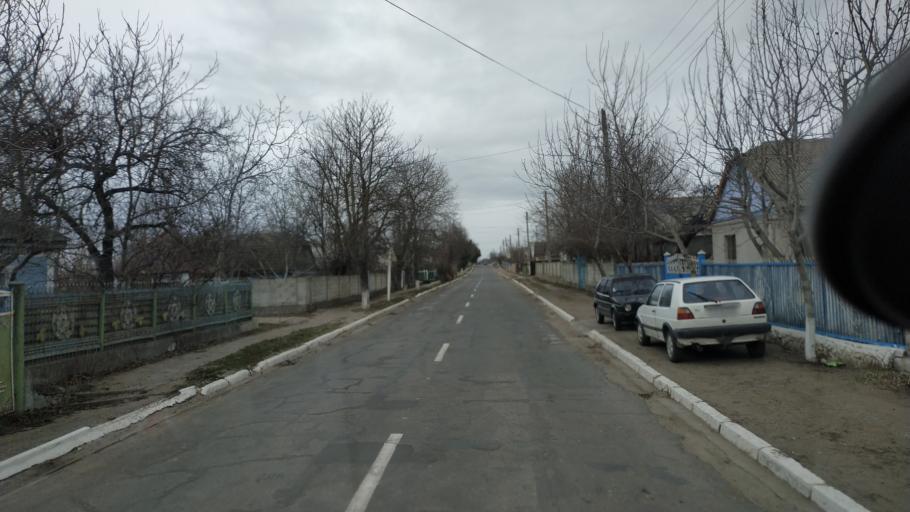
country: MD
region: Telenesti
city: Cocieri
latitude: 47.2993
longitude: 29.1146
